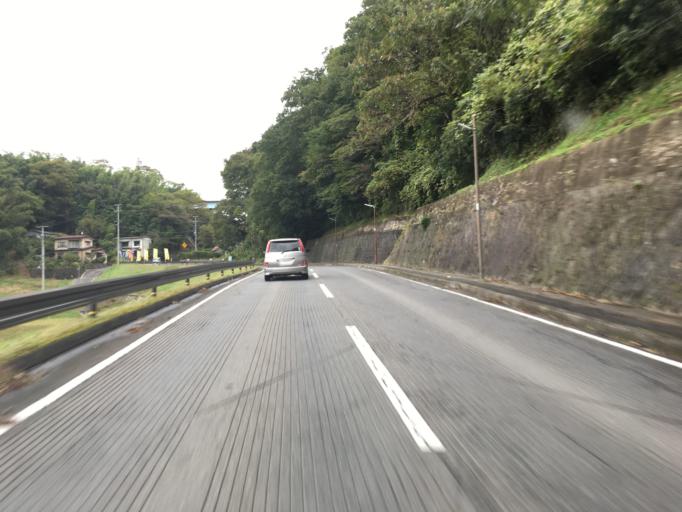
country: JP
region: Fukushima
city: Nihommatsu
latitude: 37.5935
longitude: 140.4288
